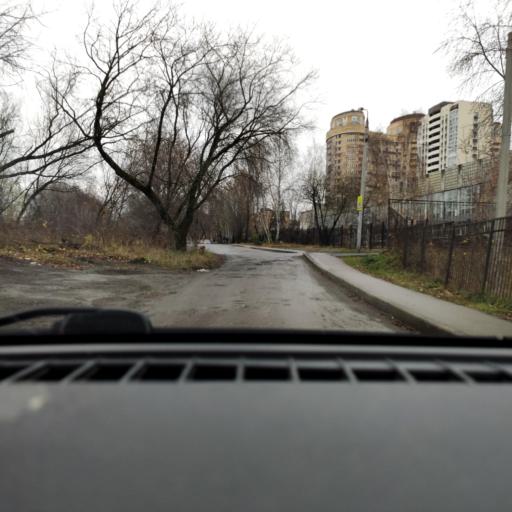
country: RU
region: Perm
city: Perm
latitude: 57.9966
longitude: 56.1990
